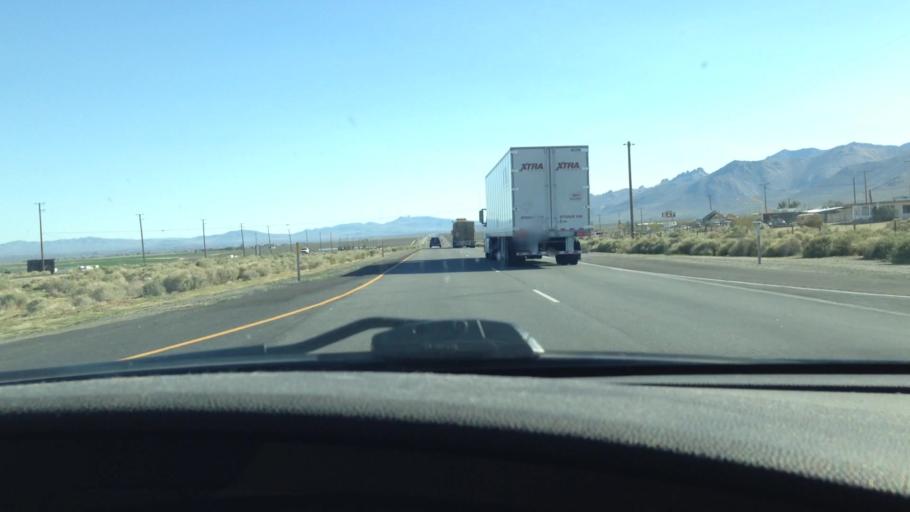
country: US
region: California
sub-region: Kern County
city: Inyokern
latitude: 35.8155
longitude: -117.8738
